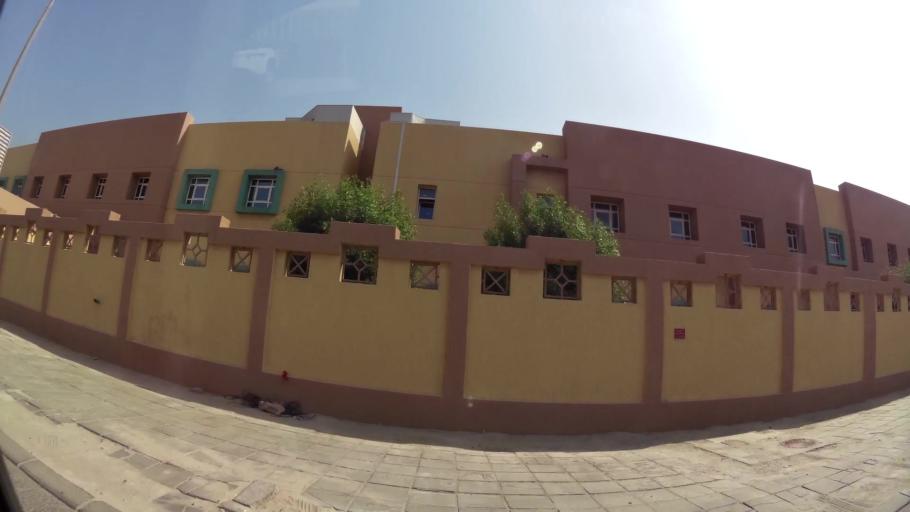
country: KW
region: Al Asimah
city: Ad Dasmah
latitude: 29.3543
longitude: 48.0197
